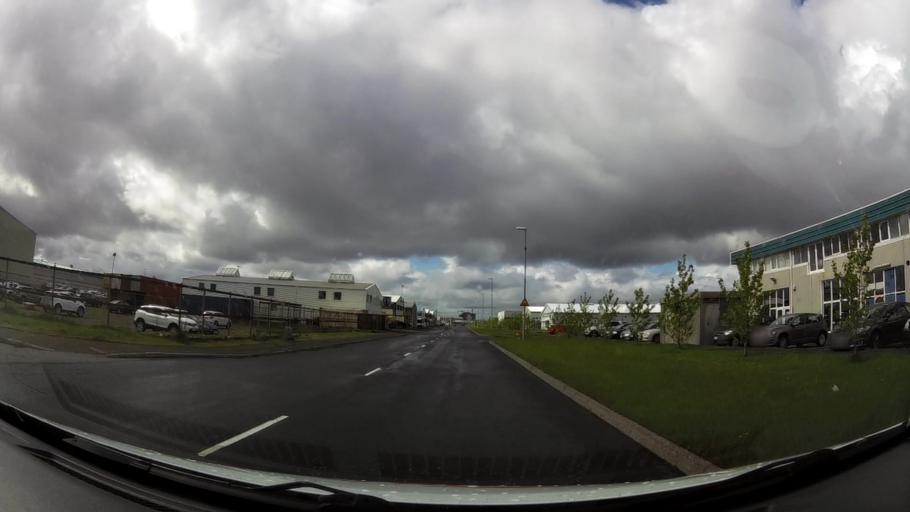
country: IS
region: Capital Region
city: Seltjarnarnes
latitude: 64.1563
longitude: -21.9439
